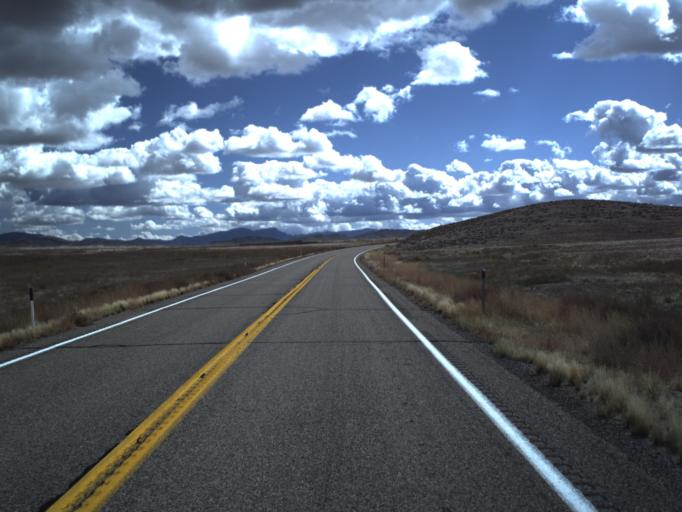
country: US
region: Nevada
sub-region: Lincoln County
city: Pioche
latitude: 38.7252
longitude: -113.9304
